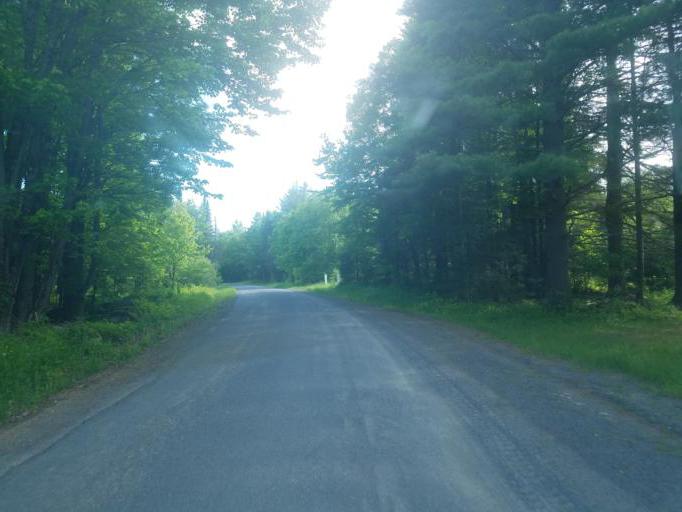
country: US
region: New York
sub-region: Herkimer County
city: Dolgeville
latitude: 43.3437
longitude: -74.9213
